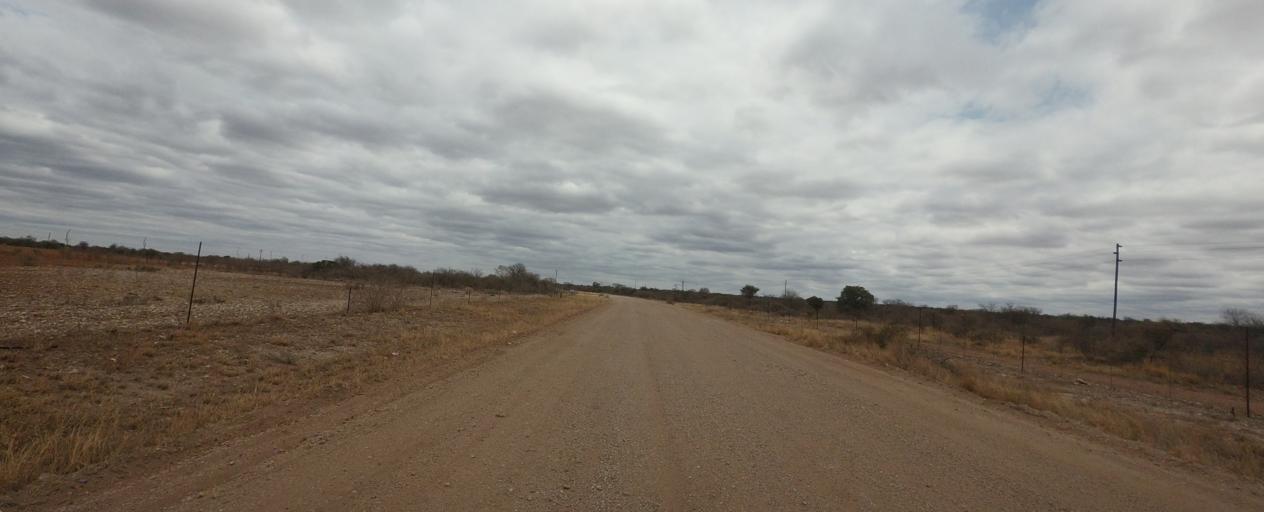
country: BW
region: Central
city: Mathathane
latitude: -22.7110
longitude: 28.5663
